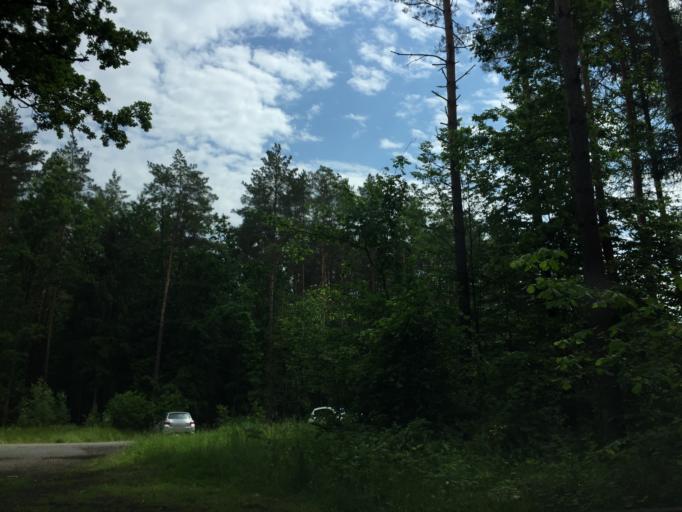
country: PL
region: Warmian-Masurian Voivodeship
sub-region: Powiat olsztynski
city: Jonkowo
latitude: 53.7669
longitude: 20.3675
